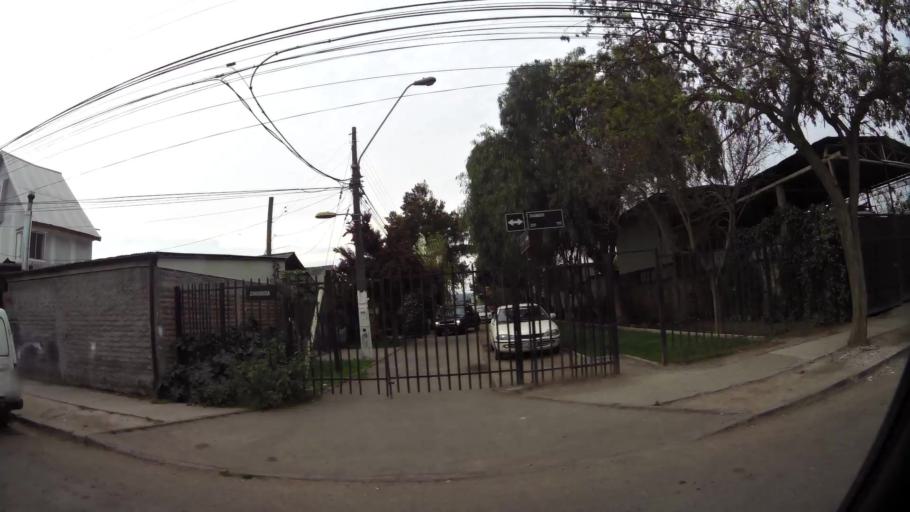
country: CL
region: Santiago Metropolitan
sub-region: Provincia de Santiago
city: Lo Prado
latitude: -33.5139
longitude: -70.7743
